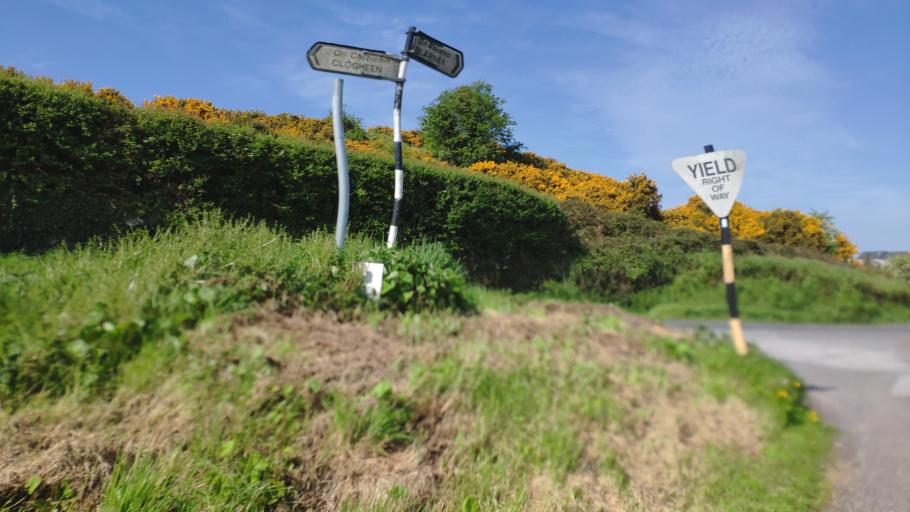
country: IE
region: Munster
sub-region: County Cork
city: Blarney
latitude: 51.9181
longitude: -8.5401
